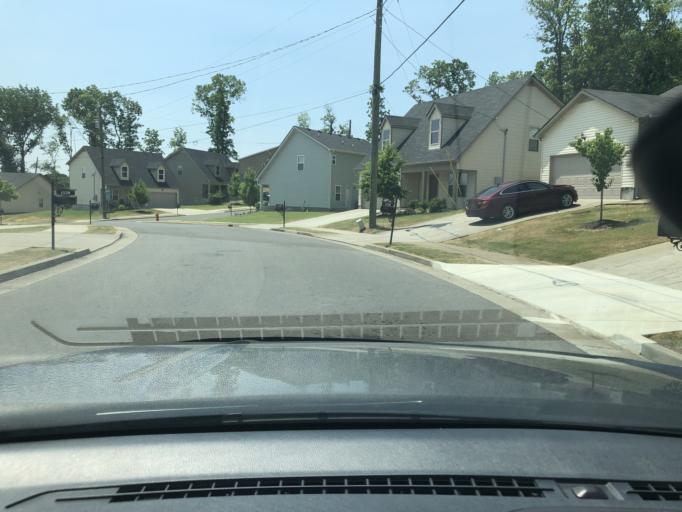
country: US
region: Tennessee
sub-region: Rutherford County
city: La Vergne
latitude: 36.0568
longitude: -86.6136
